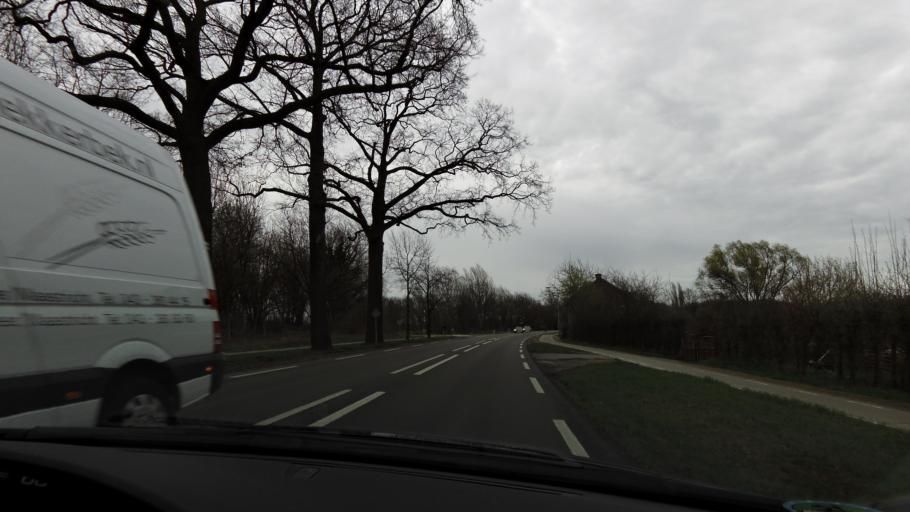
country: NL
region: Limburg
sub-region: Gemeente Maastricht
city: Heer
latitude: 50.8418
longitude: 5.7446
